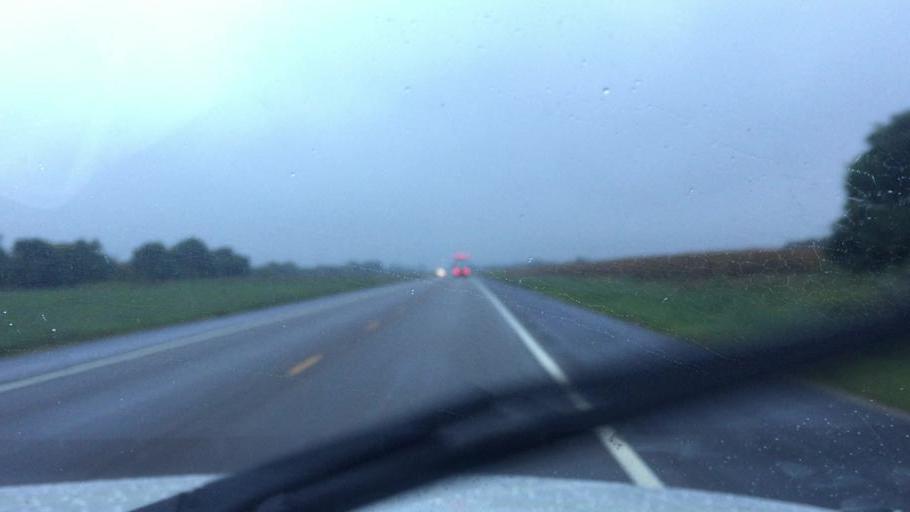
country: US
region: Kansas
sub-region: Montgomery County
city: Cherryvale
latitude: 37.4087
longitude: -95.5002
